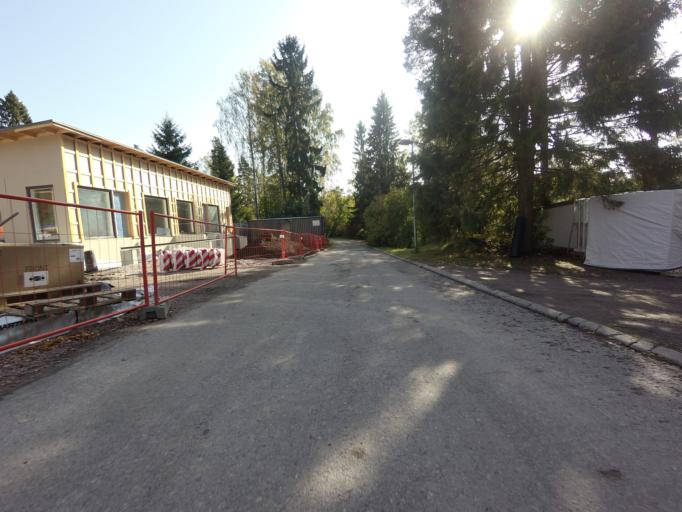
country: FI
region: Uusimaa
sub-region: Helsinki
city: Espoo
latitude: 60.1817
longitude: 24.6653
